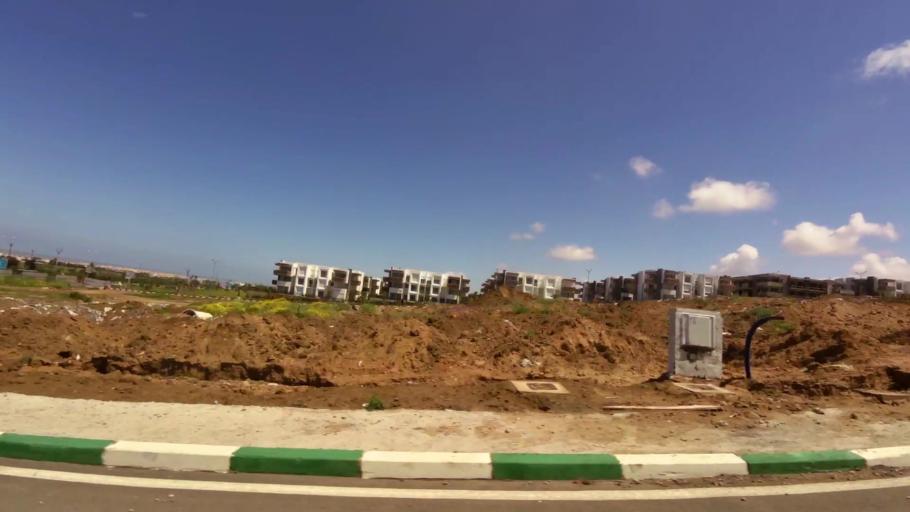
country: MA
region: Grand Casablanca
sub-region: Nouaceur
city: Dar Bouazza
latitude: 33.5250
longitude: -7.7804
